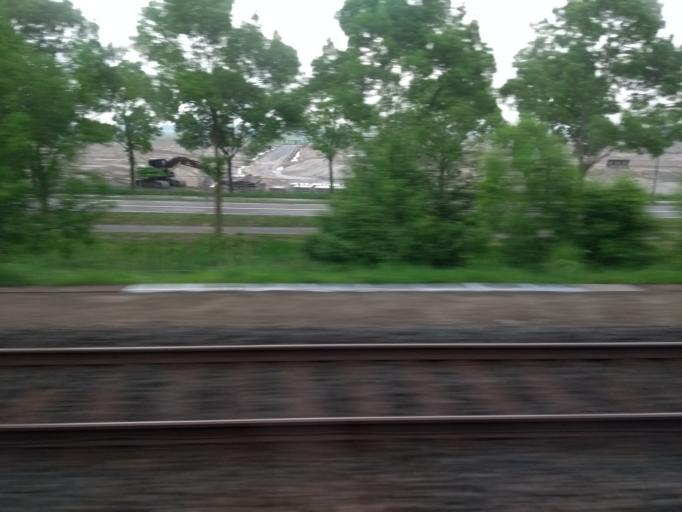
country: NL
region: North Holland
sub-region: Gemeente Weesp
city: Weesp
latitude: 52.3178
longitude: 5.0332
